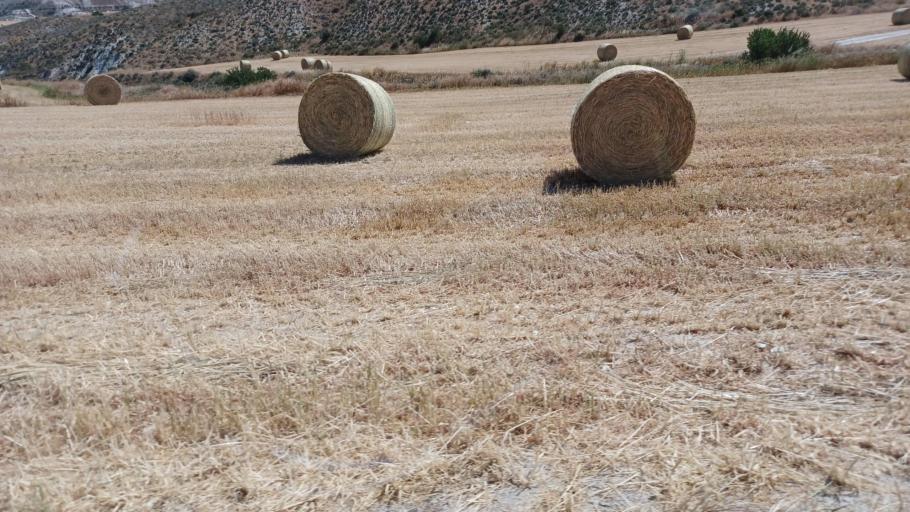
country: CY
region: Larnaka
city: Athienou
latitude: 34.9974
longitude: 33.5337
